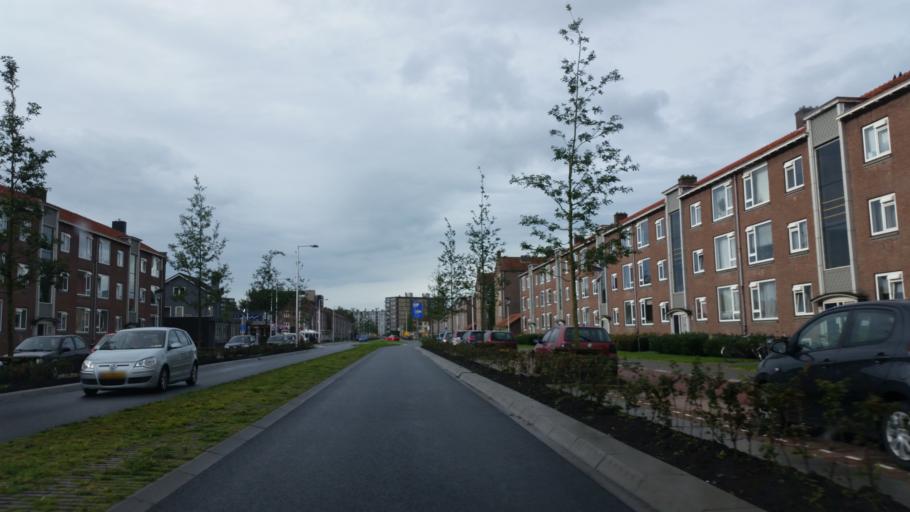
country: NL
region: Friesland
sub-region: Gemeente Leeuwarden
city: Bilgaard
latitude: 53.2096
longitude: 5.7792
